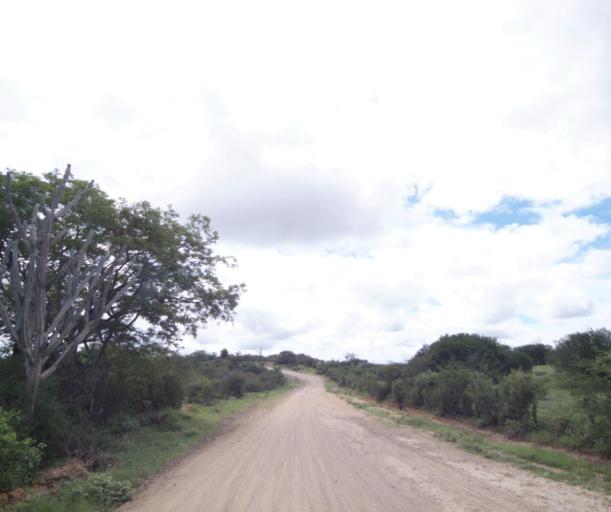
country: BR
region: Bahia
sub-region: Tanhacu
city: Tanhacu
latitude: -14.1649
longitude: -41.1694
